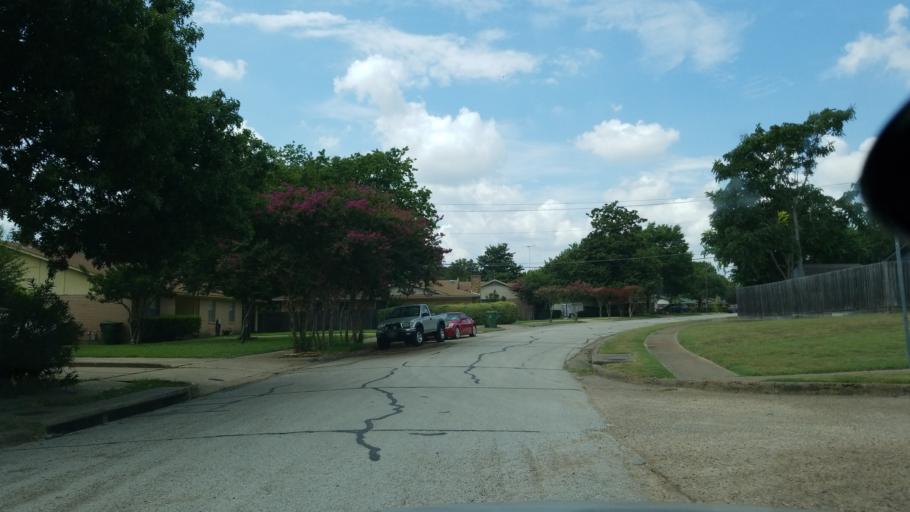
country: US
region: Texas
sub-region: Dallas County
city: Garland
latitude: 32.9138
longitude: -96.6556
